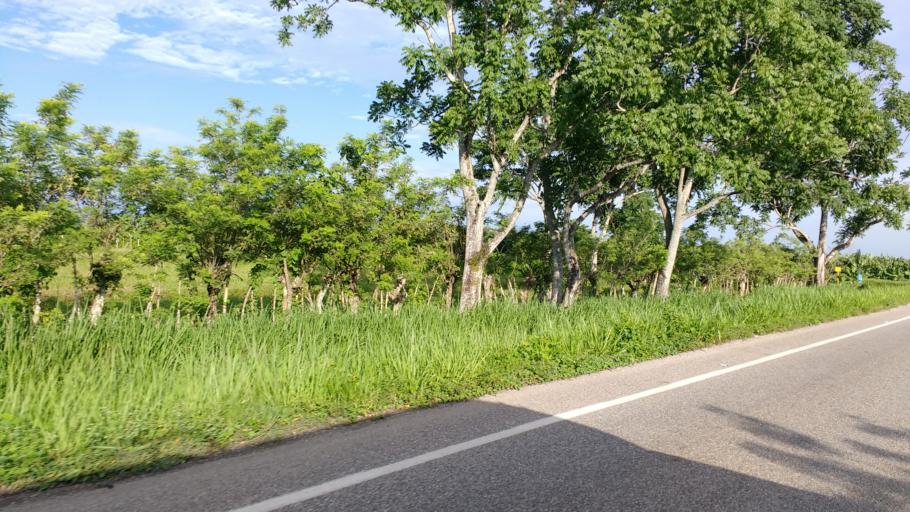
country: MX
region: Tabasco
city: Teapa
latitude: 17.6033
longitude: -92.9656
